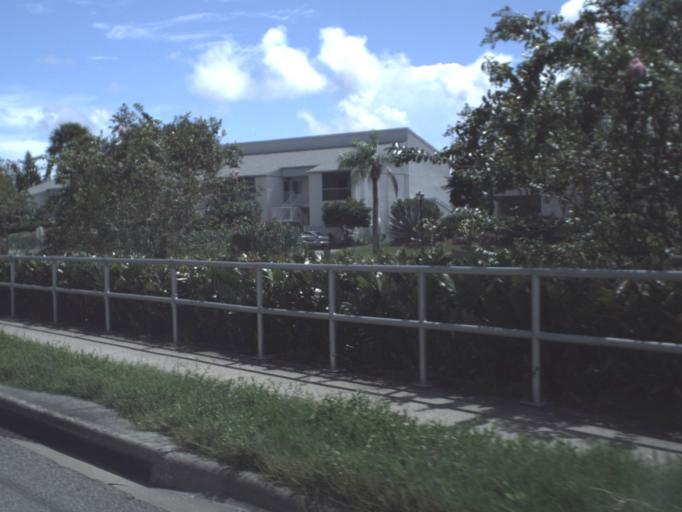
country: US
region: Florida
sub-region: Pinellas County
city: Indian Rocks Beach
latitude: 27.8820
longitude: -82.8436
